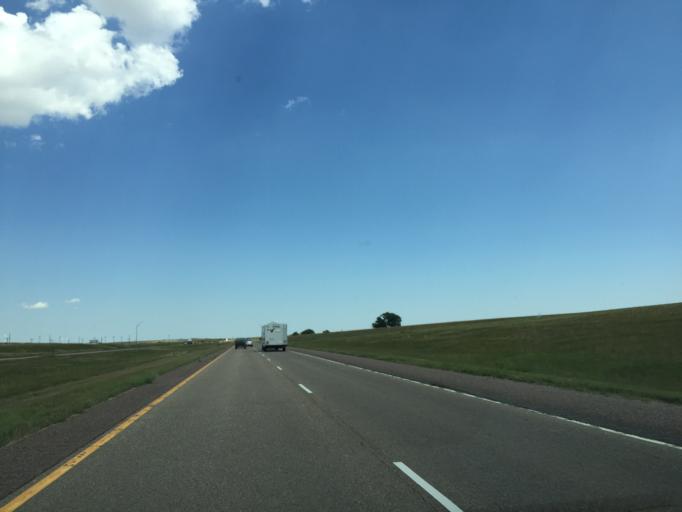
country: US
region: Colorado
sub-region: Lincoln County
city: Hugo
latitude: 39.2788
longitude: -103.3974
